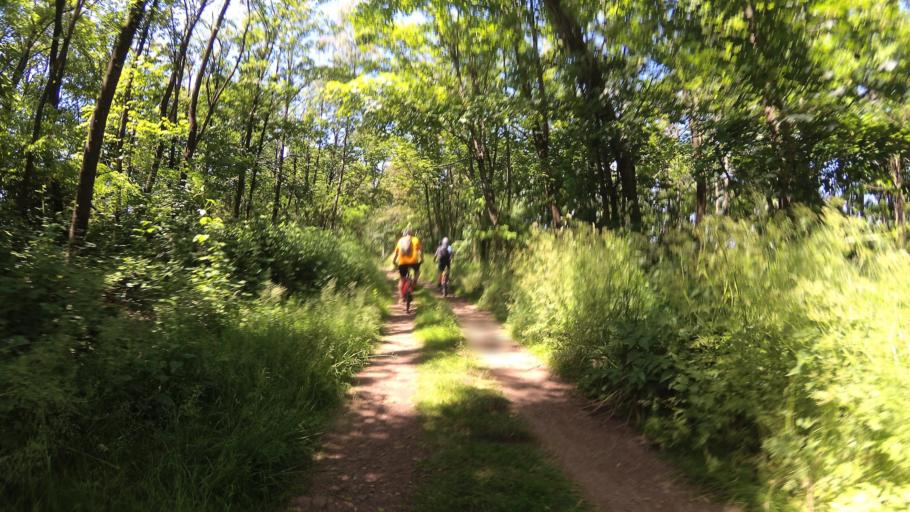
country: DE
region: Saarland
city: Lebach
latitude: 49.3792
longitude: 6.9071
